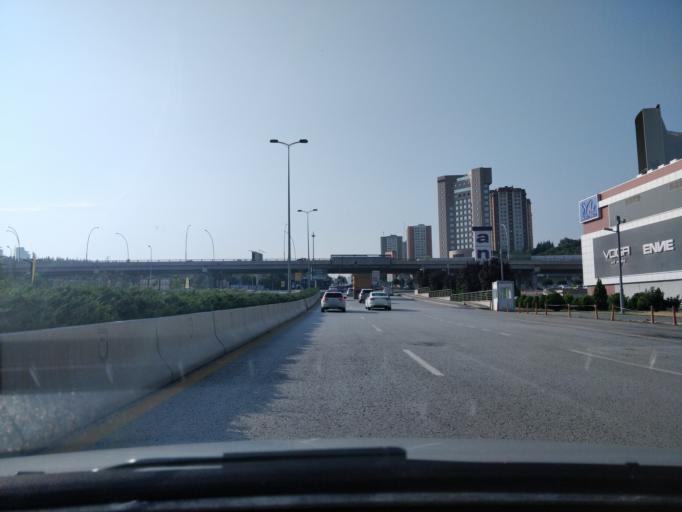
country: TR
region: Ankara
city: Etimesgut
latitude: 39.8961
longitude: 32.6779
